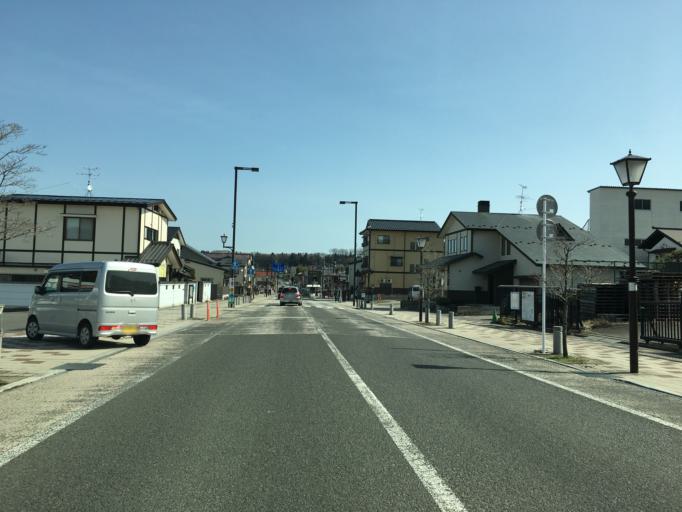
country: JP
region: Fukushima
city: Nihommatsu
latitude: 37.5994
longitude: 140.4466
